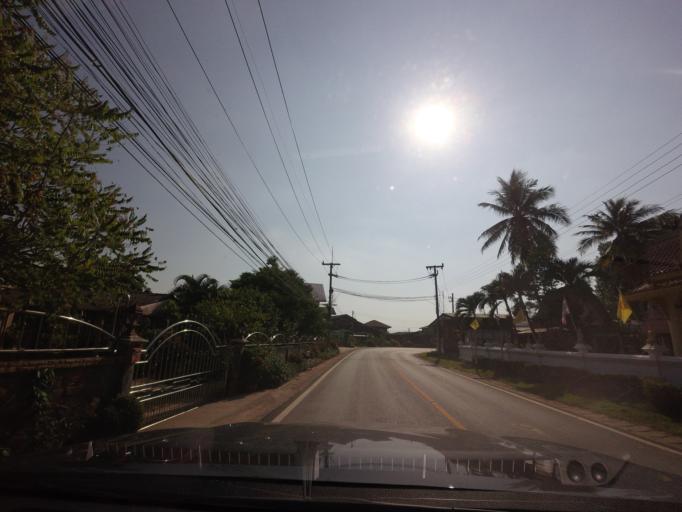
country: TH
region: Nan
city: Nan
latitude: 18.8585
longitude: 100.8177
